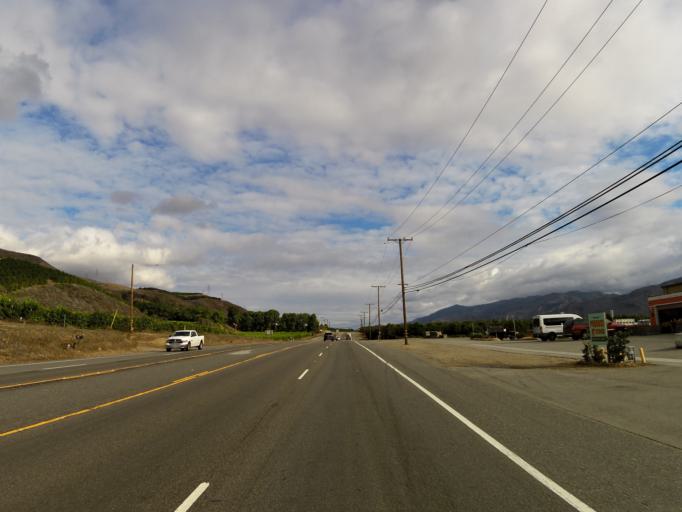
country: US
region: California
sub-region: Ventura County
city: Fillmore
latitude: 34.3955
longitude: -118.8813
